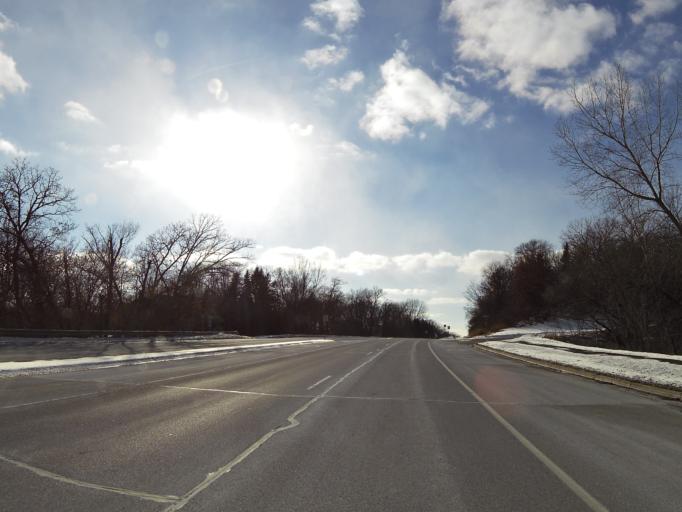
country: US
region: Minnesota
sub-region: Dakota County
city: Apple Valley
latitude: 44.7561
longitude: -93.2311
